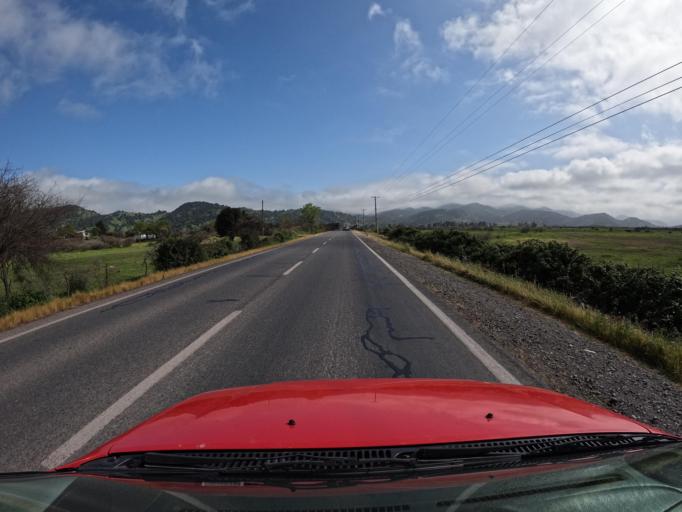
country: CL
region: Maule
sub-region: Provincia de Curico
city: Teno
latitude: -34.8387
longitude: -71.1876
